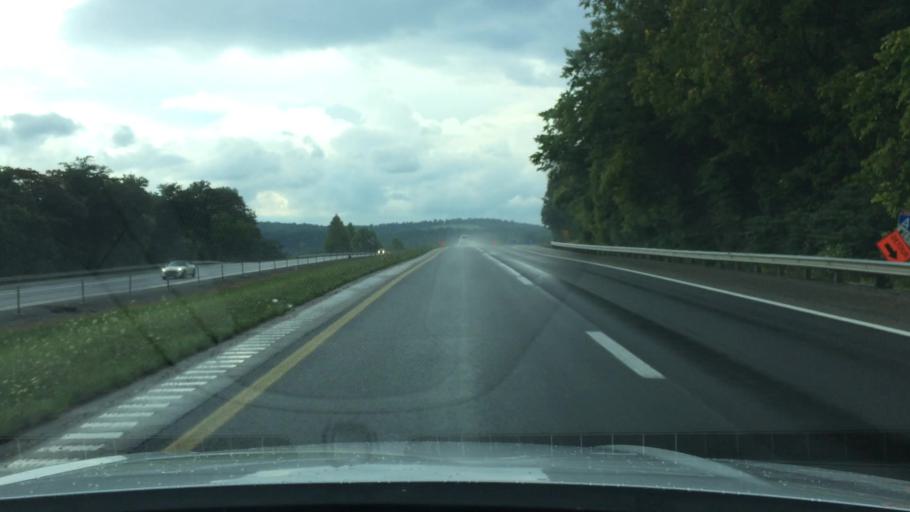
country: US
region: Tennessee
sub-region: Cocke County
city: Newport
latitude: 35.8750
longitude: -83.1856
